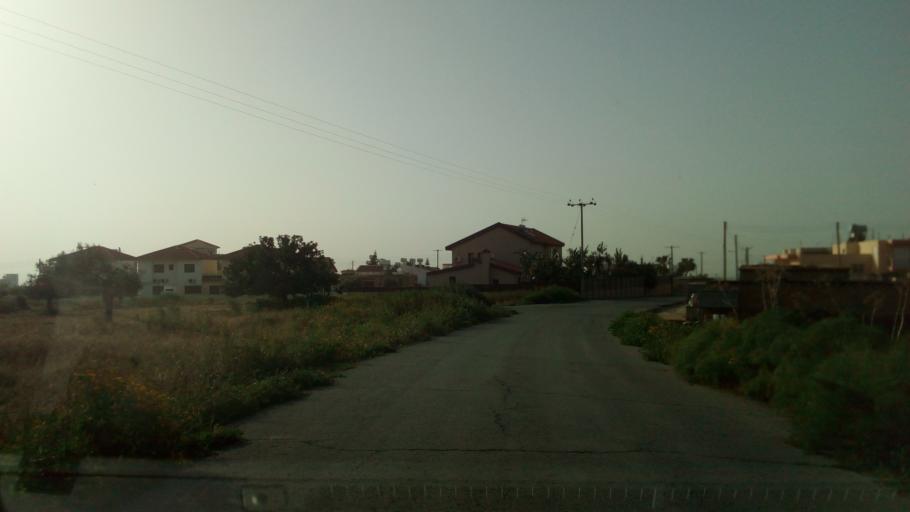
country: CY
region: Larnaka
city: Tersefanou
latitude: 34.8083
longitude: 33.4880
